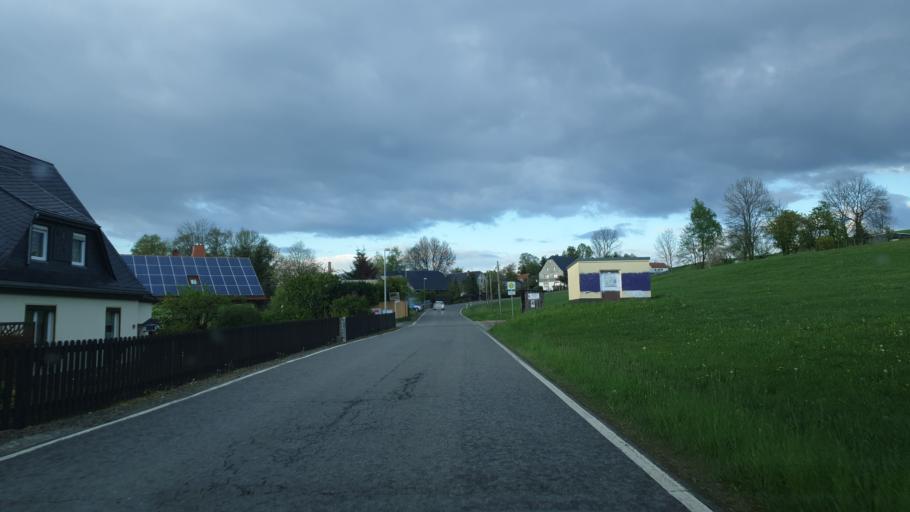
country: DE
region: Saxony
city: Hartenstein
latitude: 50.6798
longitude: 12.6915
